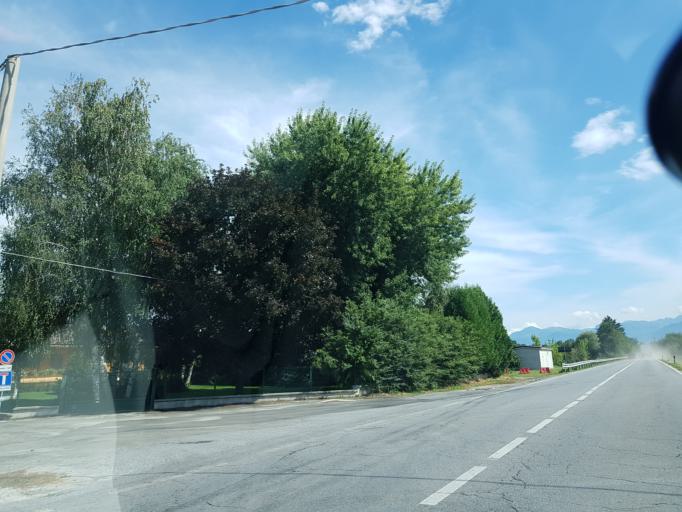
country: IT
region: Piedmont
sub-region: Provincia di Cuneo
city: Roata Rossi
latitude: 44.4584
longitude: 7.5200
